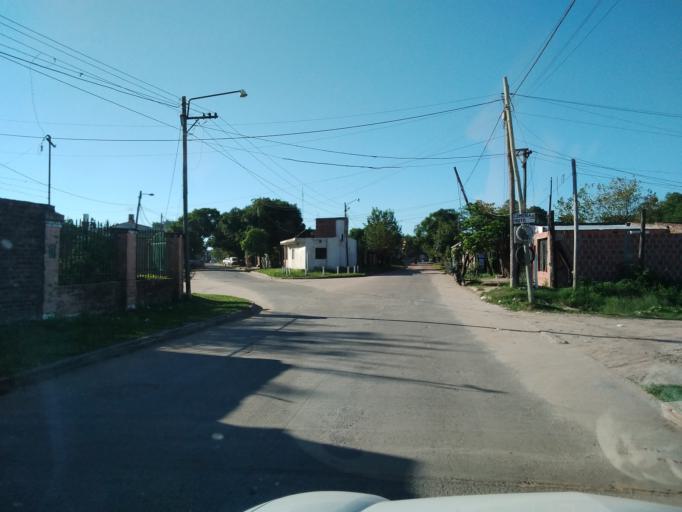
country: AR
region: Corrientes
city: Corrientes
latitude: -27.4711
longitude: -58.7961
